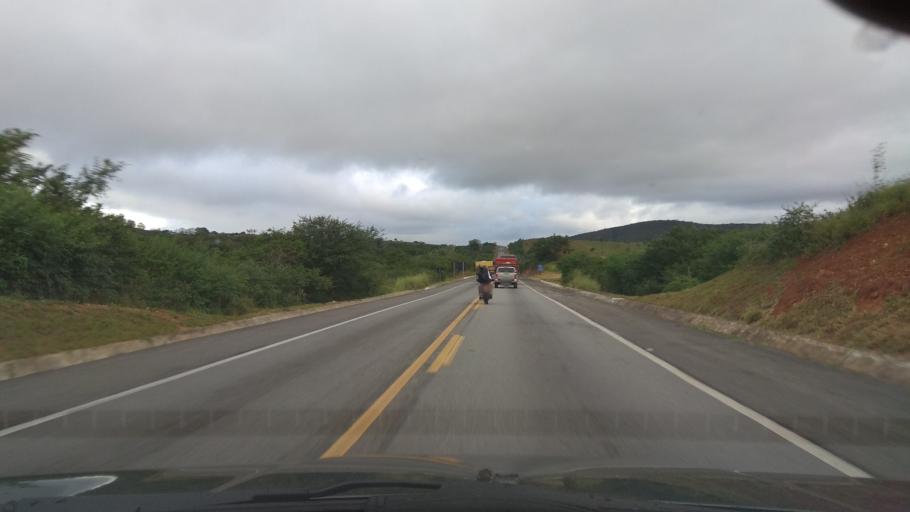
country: BR
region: Bahia
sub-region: Santa Ines
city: Santa Ines
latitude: -13.3176
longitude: -40.0171
